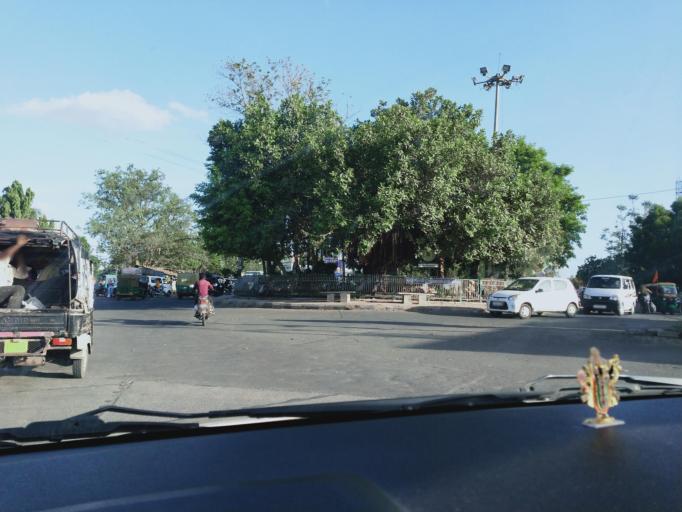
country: IN
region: Gujarat
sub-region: Bhavnagar
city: Bhavnagar
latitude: 21.7370
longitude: 72.1347
